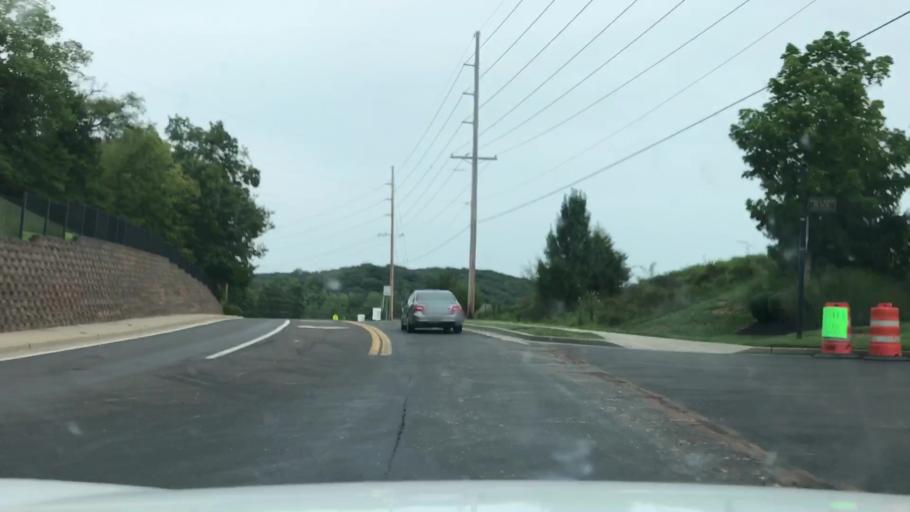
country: US
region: Missouri
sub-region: Saint Louis County
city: Clarkson Valley
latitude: 38.6472
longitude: -90.6155
